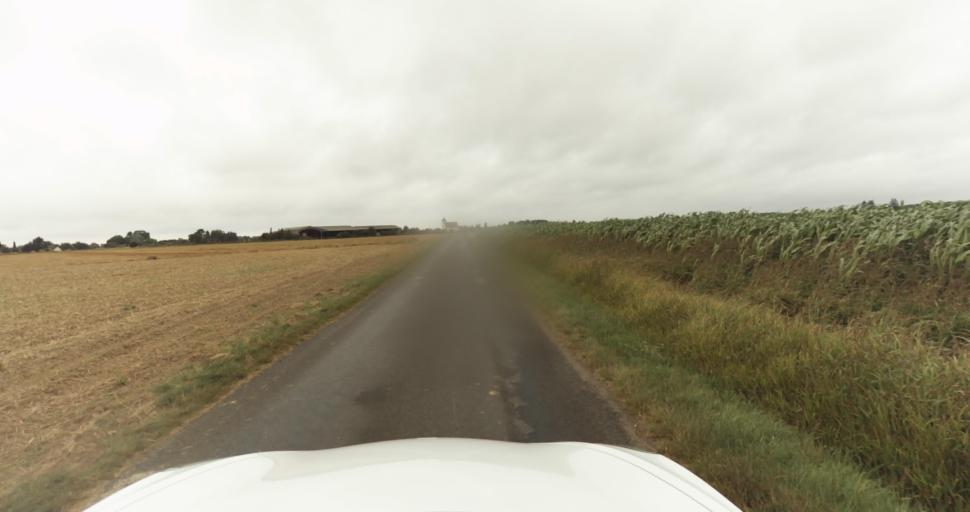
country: FR
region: Haute-Normandie
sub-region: Departement de l'Eure
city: Aviron
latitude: 49.0748
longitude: 1.0710
